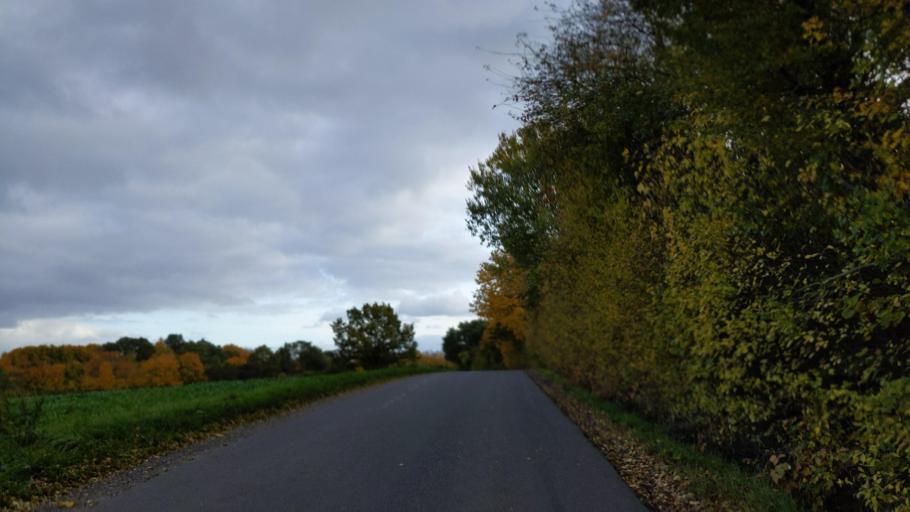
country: DE
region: Schleswig-Holstein
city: Sierksdorf
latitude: 54.0971
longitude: 10.7726
